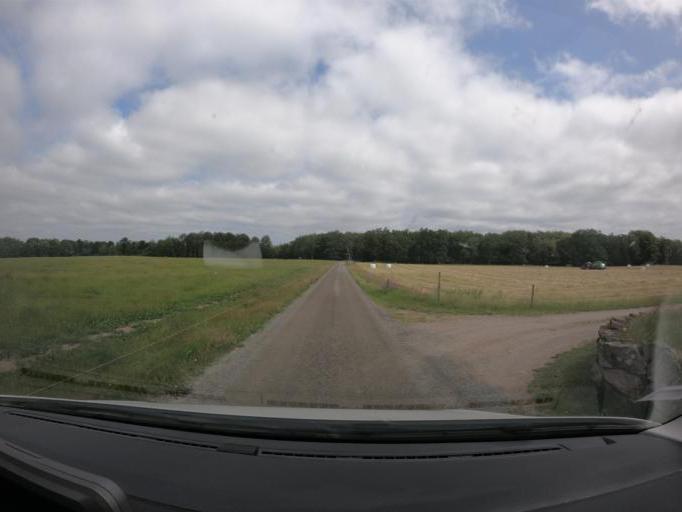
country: SE
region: Skane
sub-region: Hassleholms Kommun
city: Sosdala
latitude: 56.0666
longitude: 13.6656
